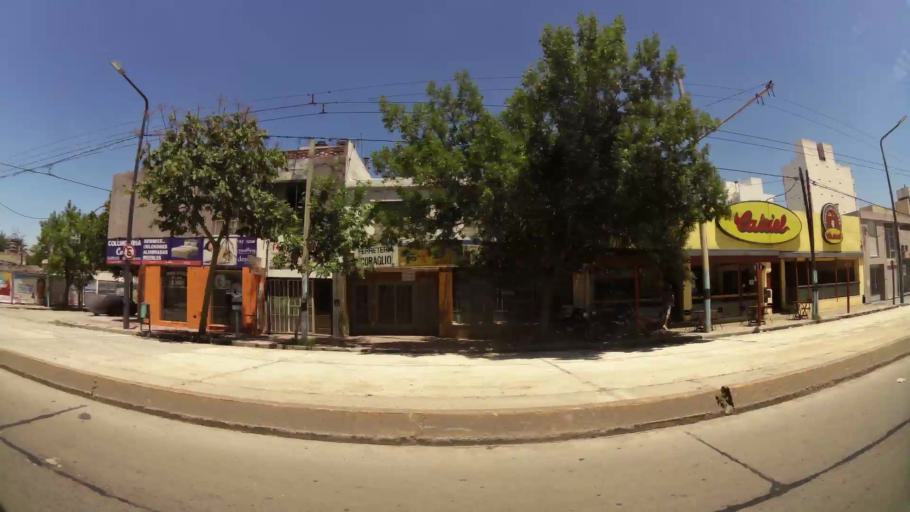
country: AR
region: Cordoba
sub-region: Departamento de Capital
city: Cordoba
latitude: -31.4037
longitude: -64.2163
